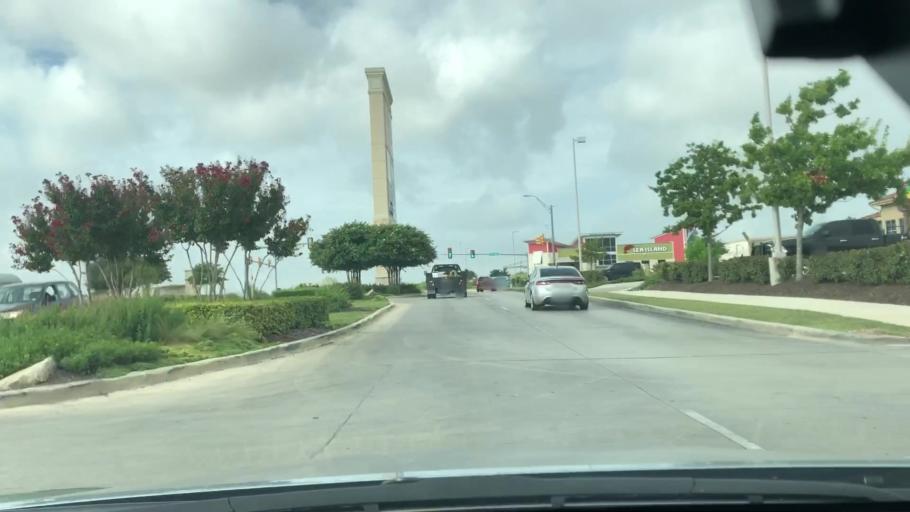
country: US
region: Texas
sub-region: Guadalupe County
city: Lake Dunlap
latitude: 29.7276
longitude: -98.0751
